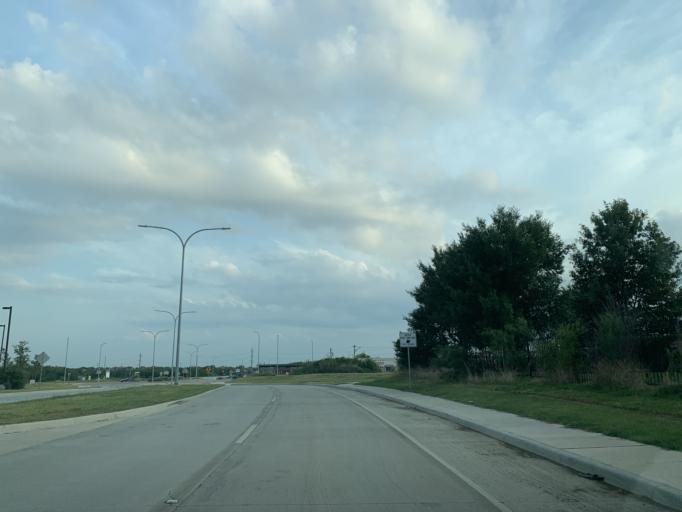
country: US
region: Texas
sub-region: Tarrant County
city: Keller
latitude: 32.9331
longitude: -97.2724
